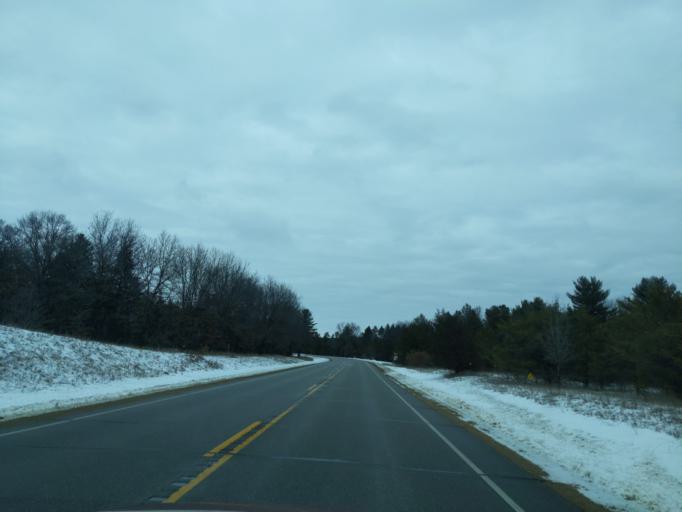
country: US
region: Wisconsin
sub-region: Waushara County
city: Wautoma
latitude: 43.9539
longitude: -89.3174
